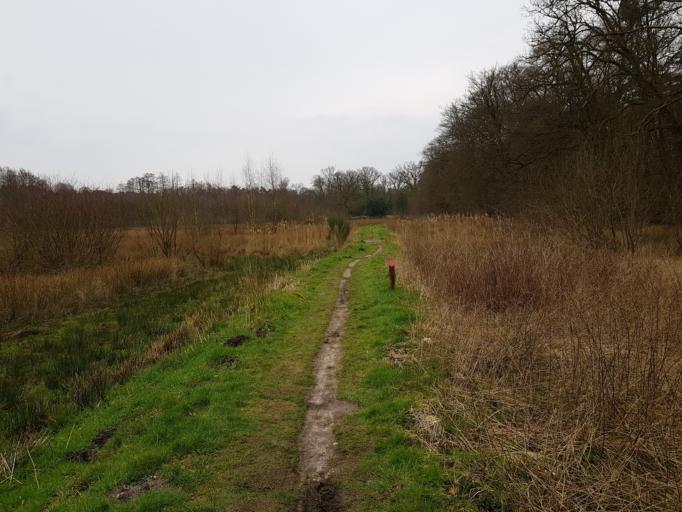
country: NL
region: Gelderland
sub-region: Gemeente Epe
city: Vaassen
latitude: 52.2862
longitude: 5.9216
